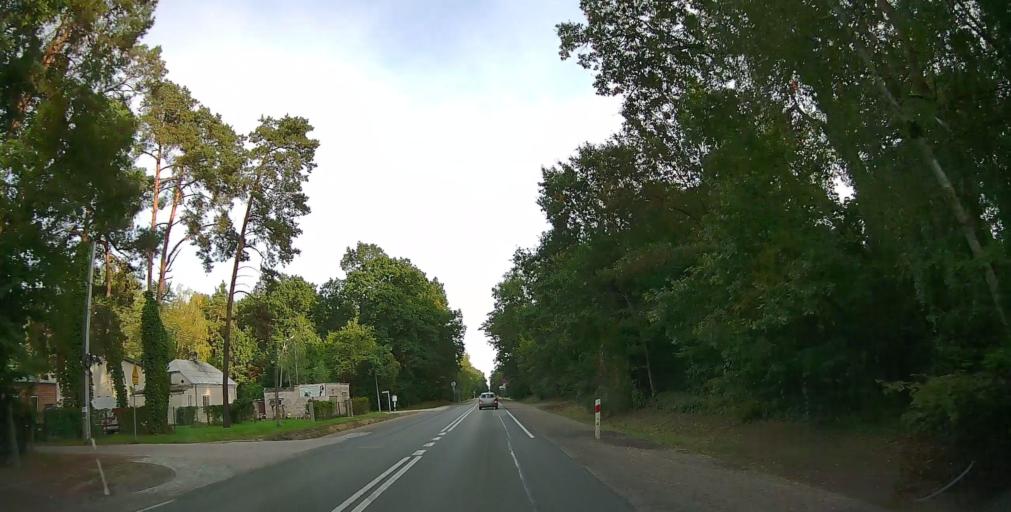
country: PL
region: Masovian Voivodeship
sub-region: Powiat piaseczynski
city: Zabieniec
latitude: 52.0510
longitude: 21.0643
